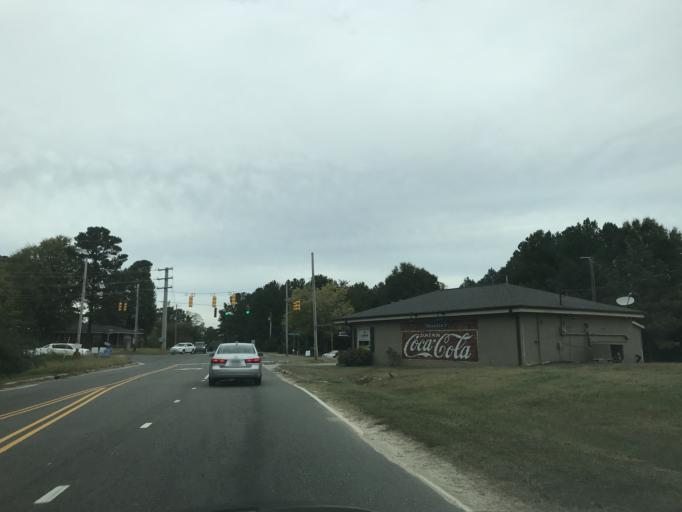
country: US
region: North Carolina
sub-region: Wake County
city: Rolesville
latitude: 35.9249
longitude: -78.5042
